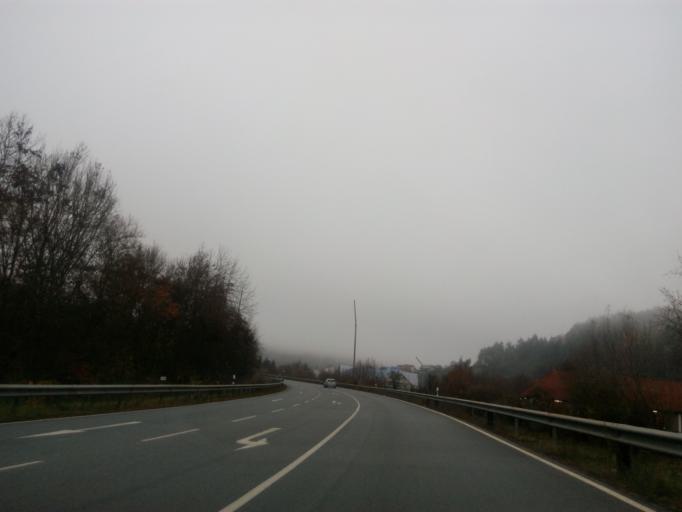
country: DE
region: Rheinland-Pfalz
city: Lauterecken
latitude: 49.6433
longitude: 7.5979
